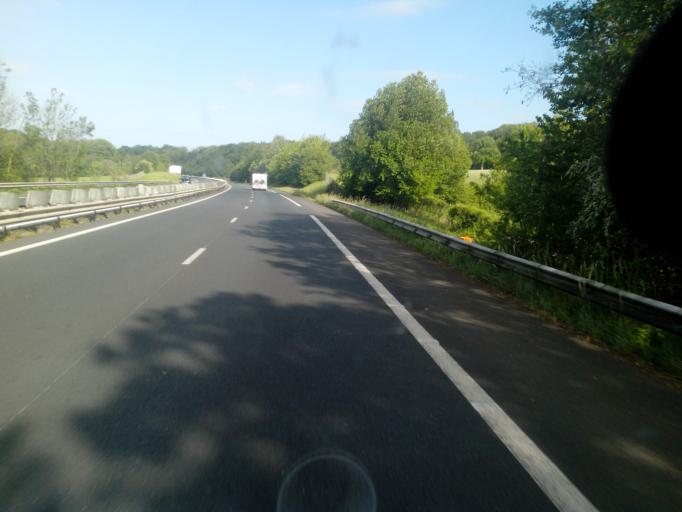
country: FR
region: Lower Normandy
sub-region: Departement du Calvados
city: Dozule
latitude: 49.2469
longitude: 0.0348
